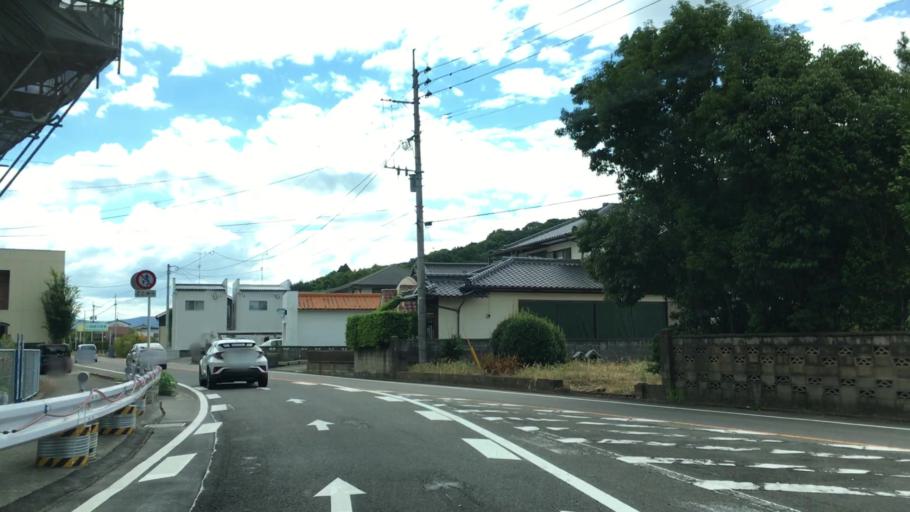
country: JP
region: Saga Prefecture
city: Saga-shi
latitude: 33.2226
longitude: 130.1725
